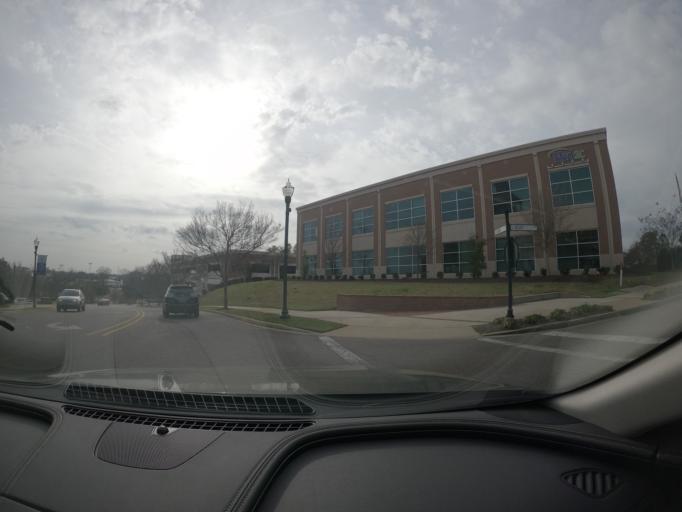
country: US
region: South Carolina
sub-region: Aiken County
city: North Augusta
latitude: 33.4896
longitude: -81.9731
